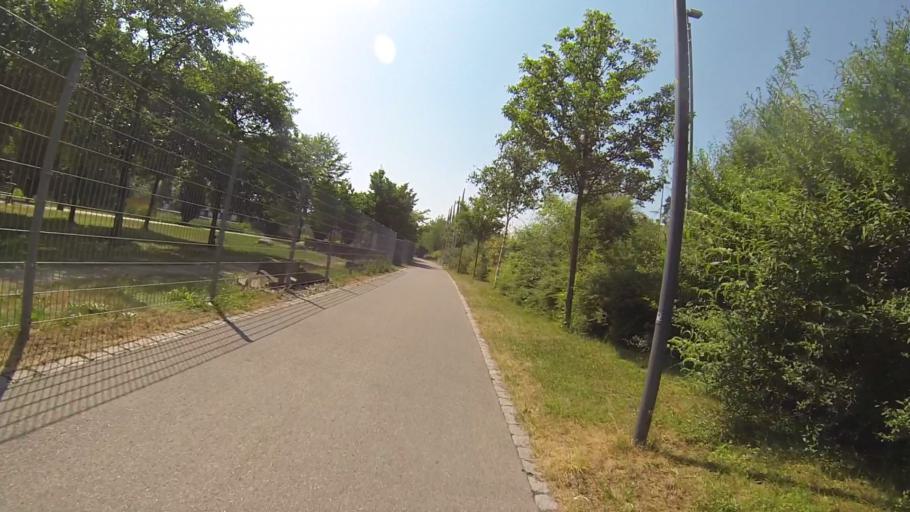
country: DE
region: Baden-Wuerttemberg
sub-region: Regierungsbezirk Stuttgart
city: Heidenheim an der Brenz
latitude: 48.6857
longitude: 10.1549
